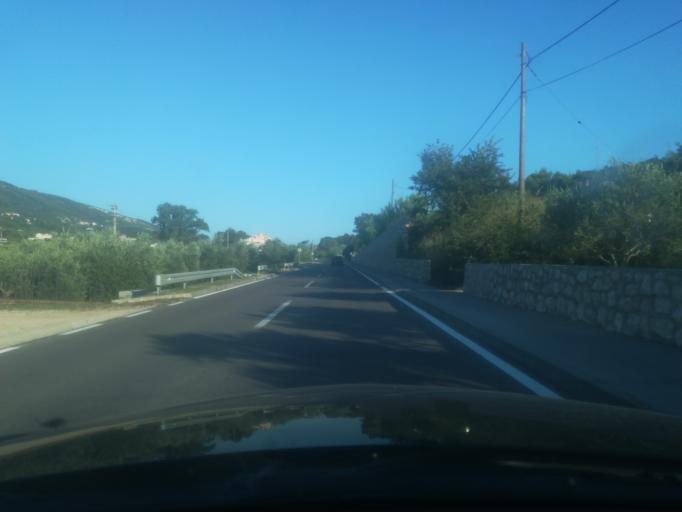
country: HR
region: Primorsko-Goranska
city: Kampor
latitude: 44.7777
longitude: 14.7531
